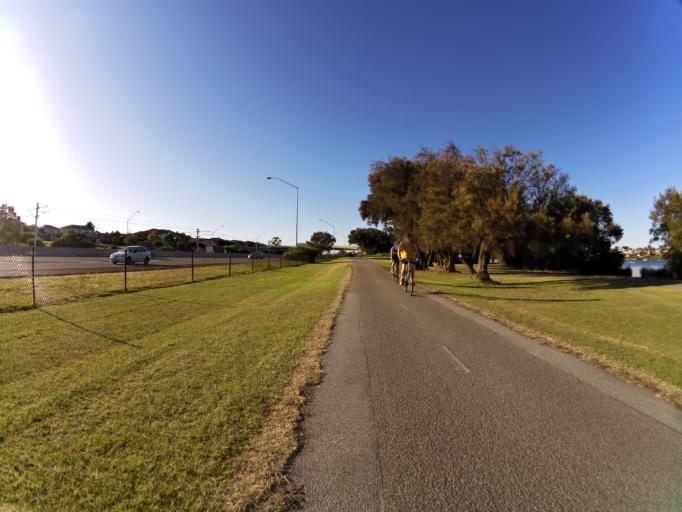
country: AU
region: Western Australia
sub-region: South Perth
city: Manning
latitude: -32.0159
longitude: 115.8572
